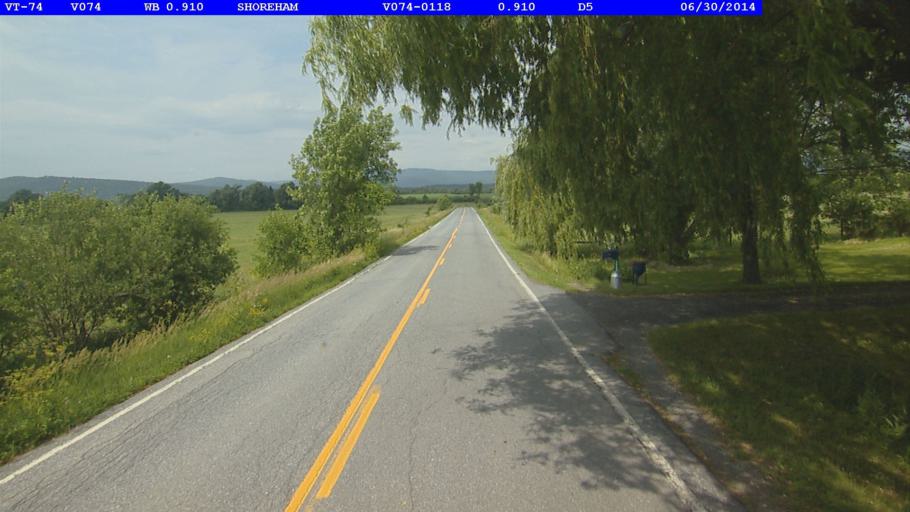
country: US
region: New York
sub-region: Essex County
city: Ticonderoga
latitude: 43.8555
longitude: -73.3591
